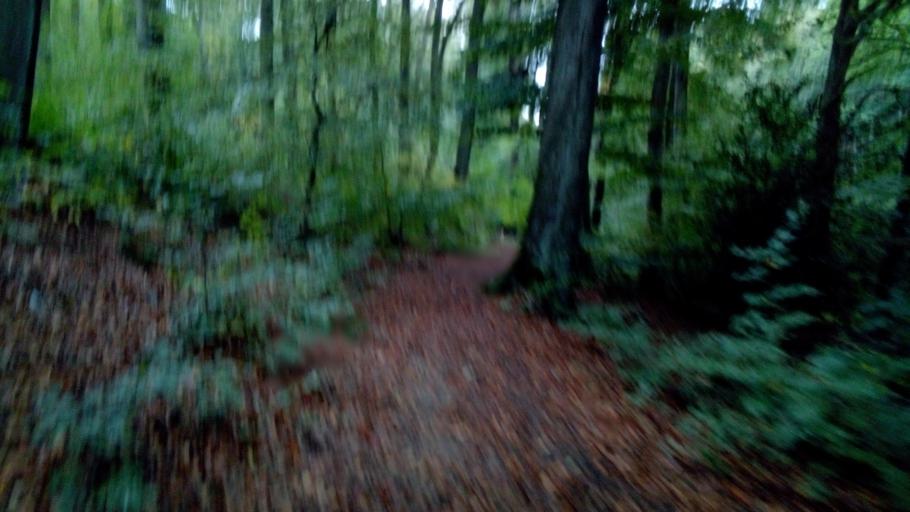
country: DE
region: North Rhine-Westphalia
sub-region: Regierungsbezirk Arnsberg
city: Bochum
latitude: 51.4433
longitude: 7.2524
